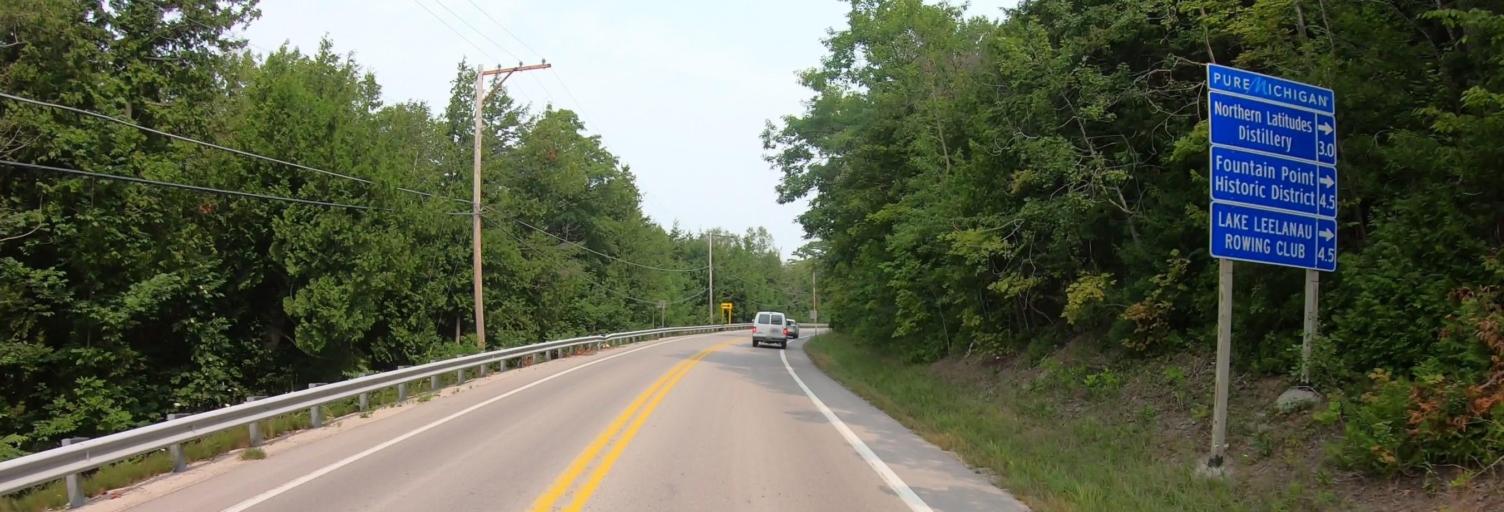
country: US
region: Michigan
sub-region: Leelanau County
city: Leland
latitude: 44.9921
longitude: -85.7700
